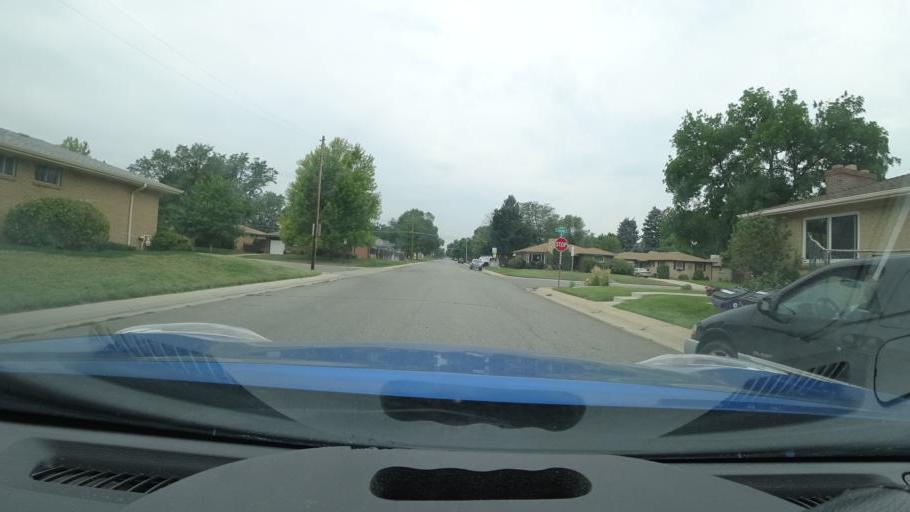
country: US
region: Colorado
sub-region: Arapahoe County
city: Glendale
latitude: 39.6876
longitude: -104.9137
